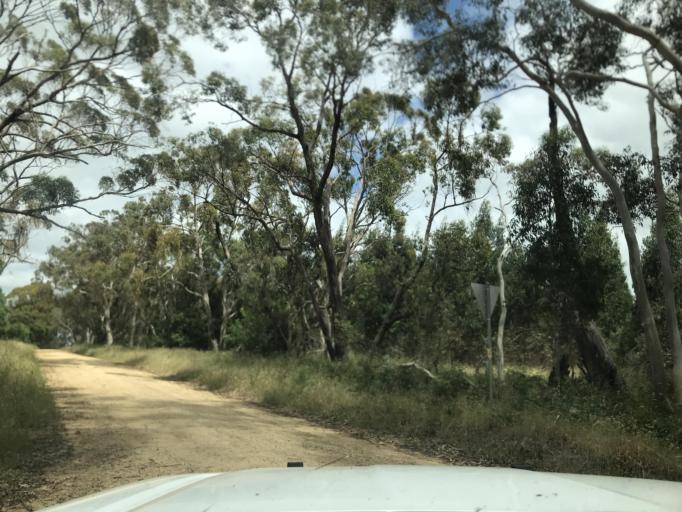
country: AU
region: South Australia
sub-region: Wattle Range
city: Penola
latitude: -37.2975
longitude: 141.0086
